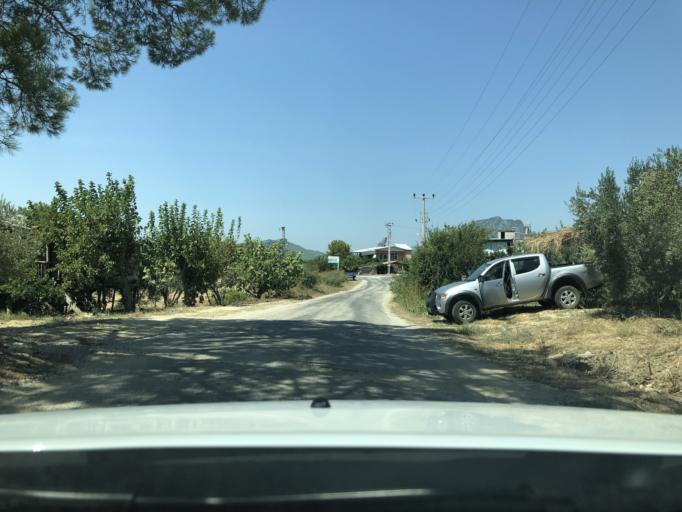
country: TR
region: Antalya
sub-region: Manavgat
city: Kizilagac
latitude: 36.8566
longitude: 31.5639
